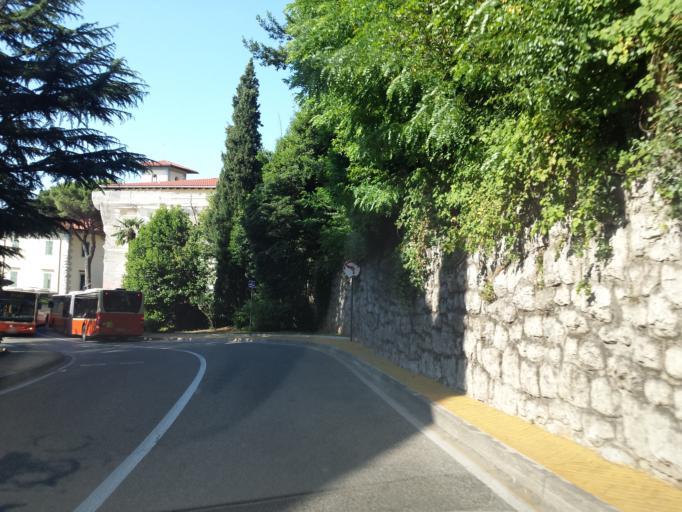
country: HR
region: Primorsko-Goranska
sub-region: Grad Opatija
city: Opatija
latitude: 45.3463
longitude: 14.3176
